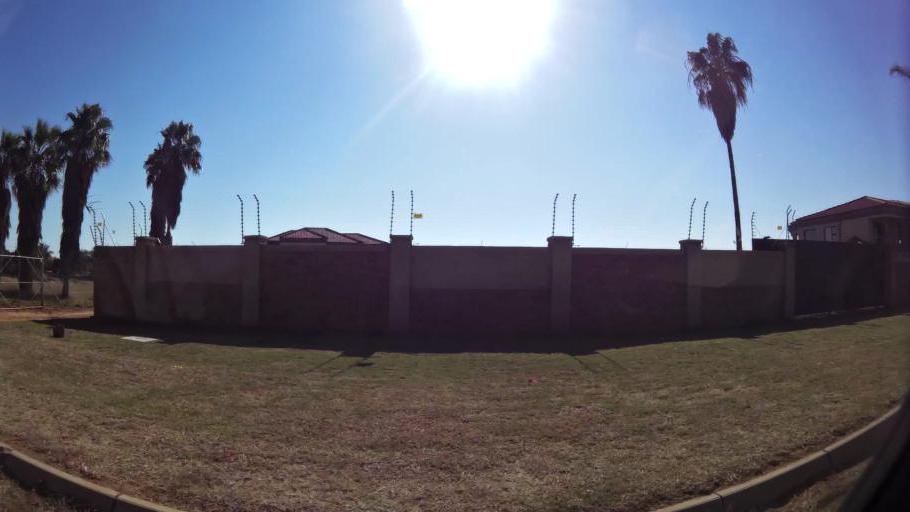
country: ZA
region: North-West
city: Ga-Rankuwa
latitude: -25.6507
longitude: 28.0814
